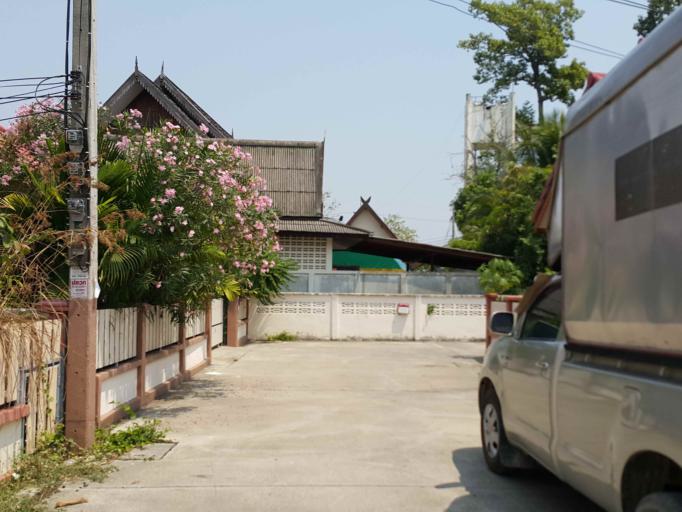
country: TH
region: Chiang Mai
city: San Kamphaeng
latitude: 18.7917
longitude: 99.0928
